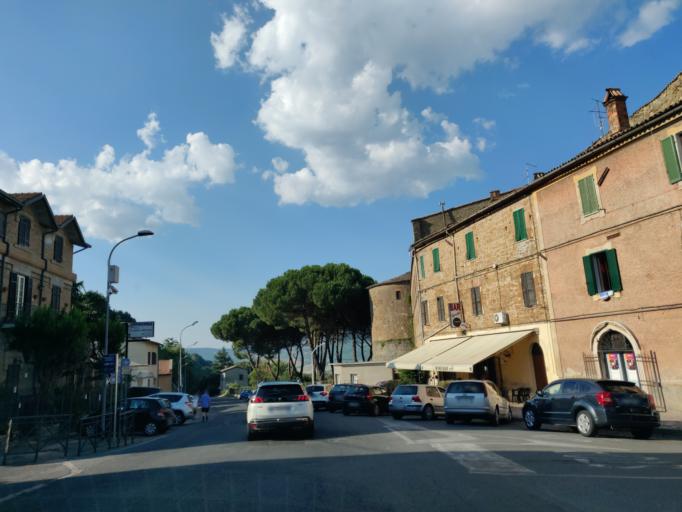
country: IT
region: Latium
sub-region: Provincia di Viterbo
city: Acquapendente
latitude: 42.7464
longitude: 11.8632
